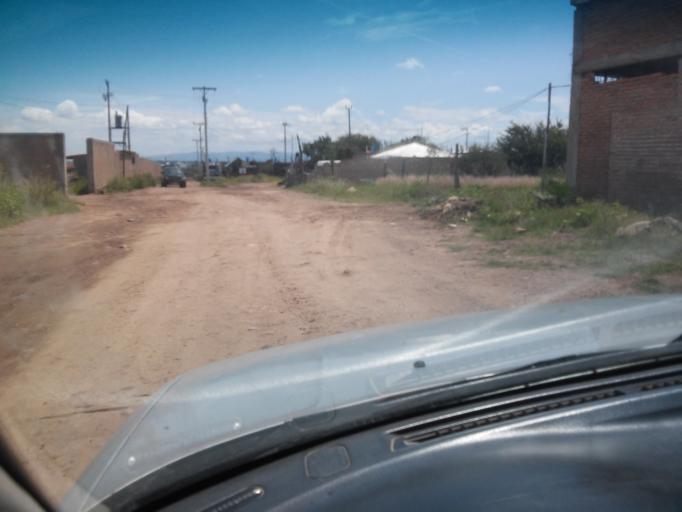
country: MX
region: Durango
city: Victoria de Durango
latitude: 23.9840
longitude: -104.7068
